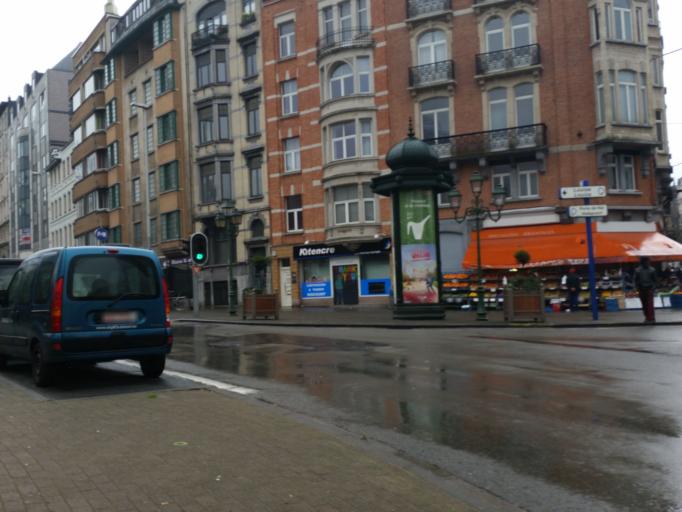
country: BE
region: Brussels Capital
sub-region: Bruxelles-Capitale
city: Brussels
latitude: 50.8330
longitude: 4.3429
